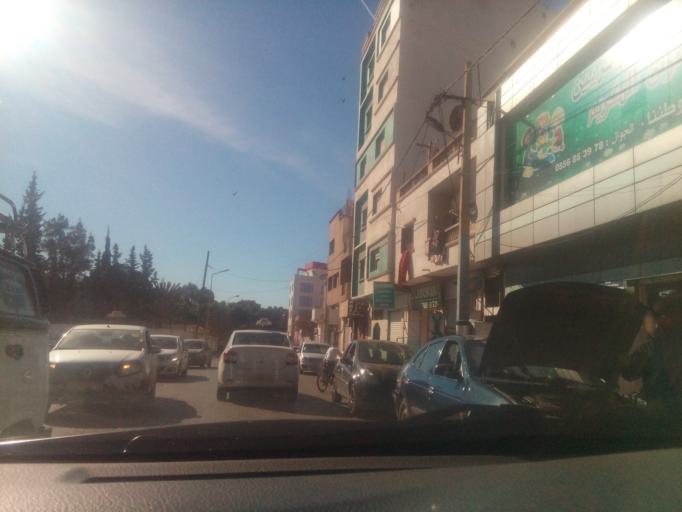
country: DZ
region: Oran
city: Oran
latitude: 35.7031
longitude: -0.6072
